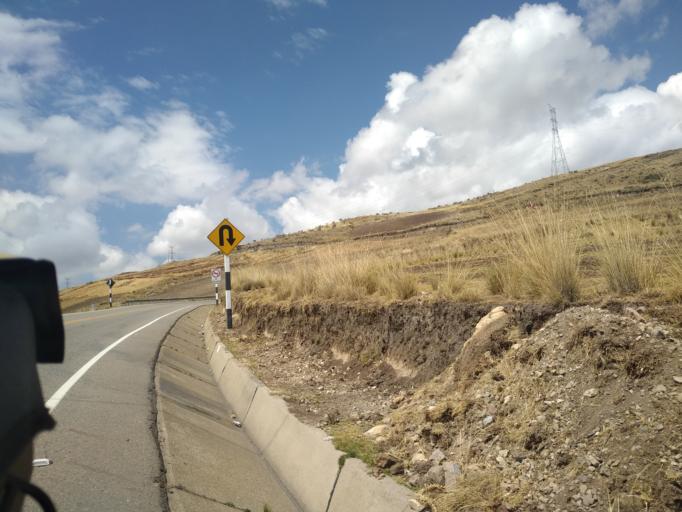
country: PE
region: La Libertad
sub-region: Provincia de Santiago de Chuco
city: Quiruvilca
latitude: -7.9180
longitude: -78.1516
